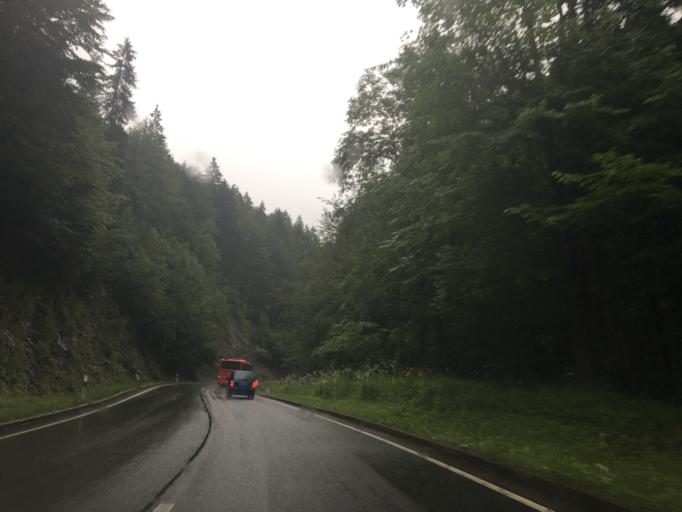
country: DE
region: Bavaria
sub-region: Upper Bavaria
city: Reit im Winkl
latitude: 47.7008
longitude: 12.4783
